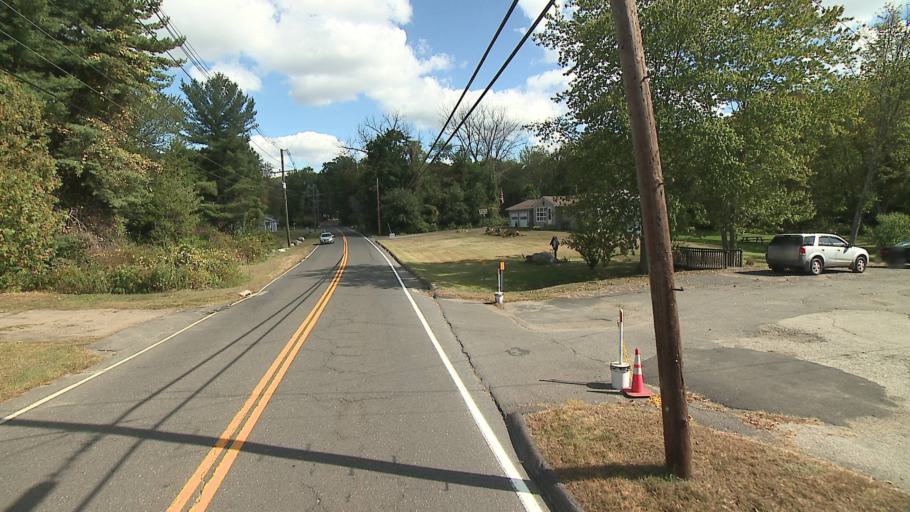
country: US
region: Connecticut
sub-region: New Haven County
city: Naugatuck
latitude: 41.4386
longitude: -73.0438
